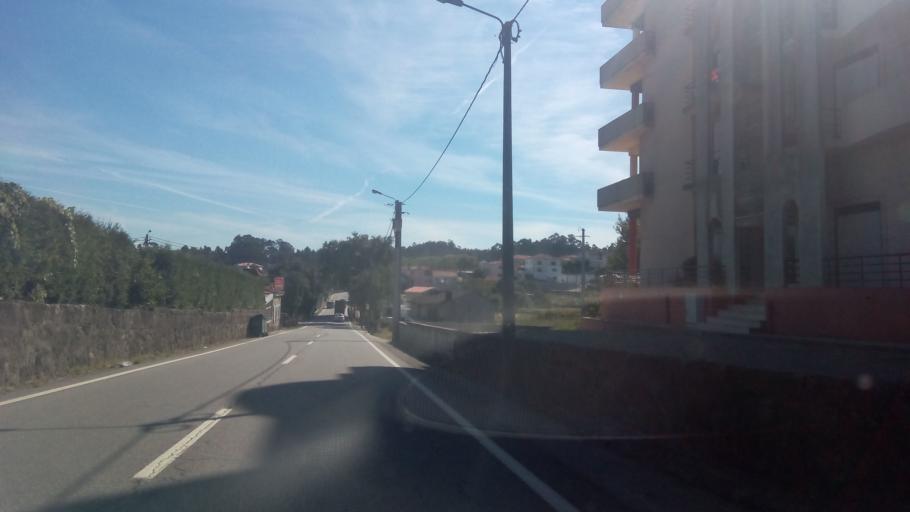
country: PT
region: Porto
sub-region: Paredes
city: Baltar
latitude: 41.1867
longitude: -8.3893
